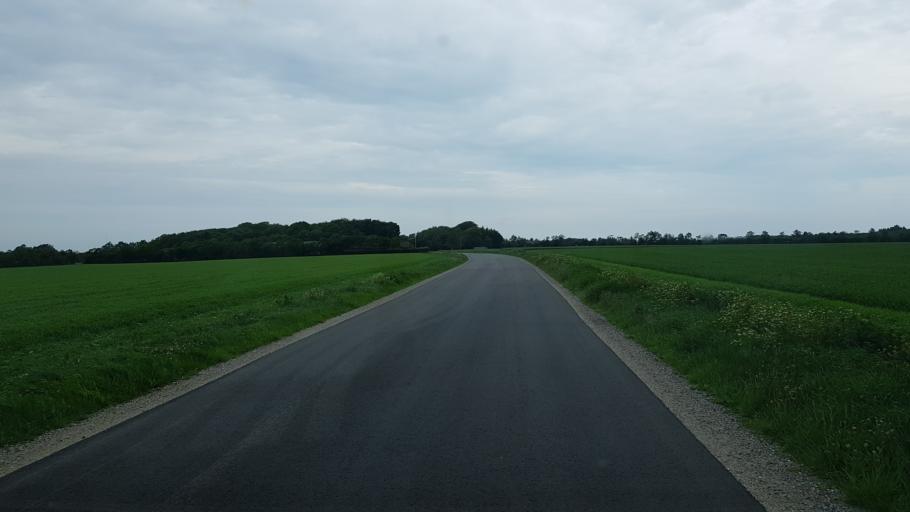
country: DK
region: South Denmark
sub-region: Varde Kommune
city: Oksbol
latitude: 55.7401
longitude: 8.3741
